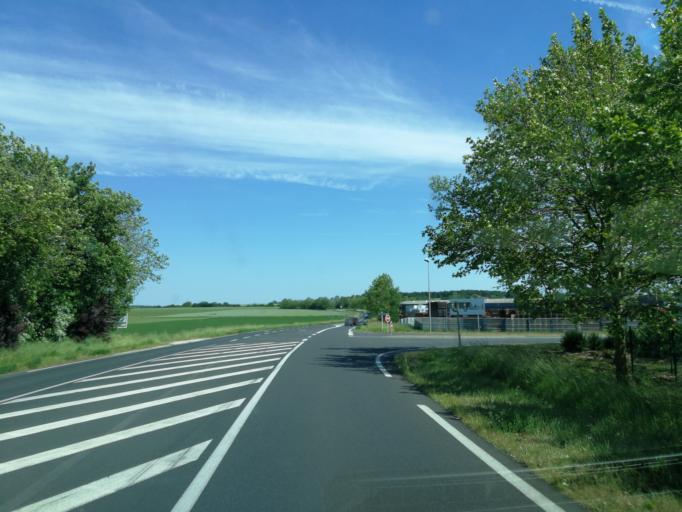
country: FR
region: Poitou-Charentes
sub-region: Departement de la Vienne
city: Loudun
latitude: 47.0229
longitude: 0.0937
